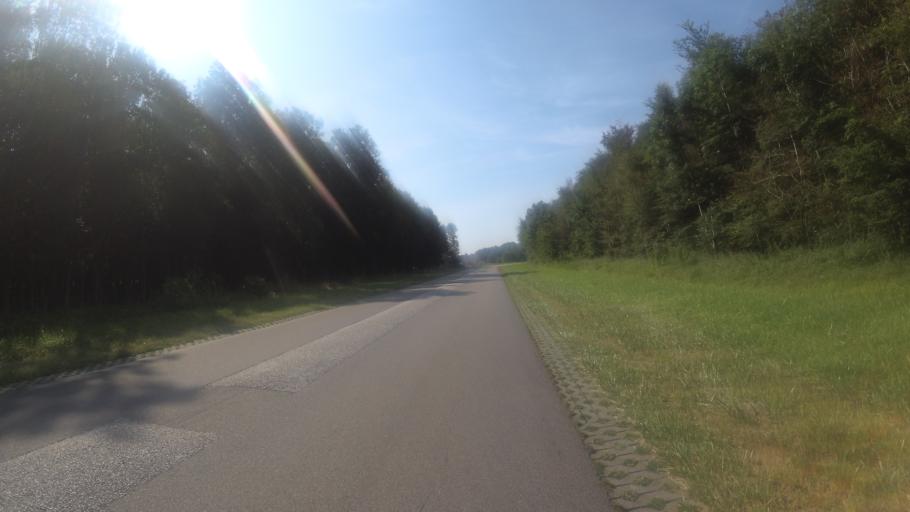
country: NL
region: Zeeland
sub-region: Gemeente Veere
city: Veere
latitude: 51.5792
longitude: 3.6611
